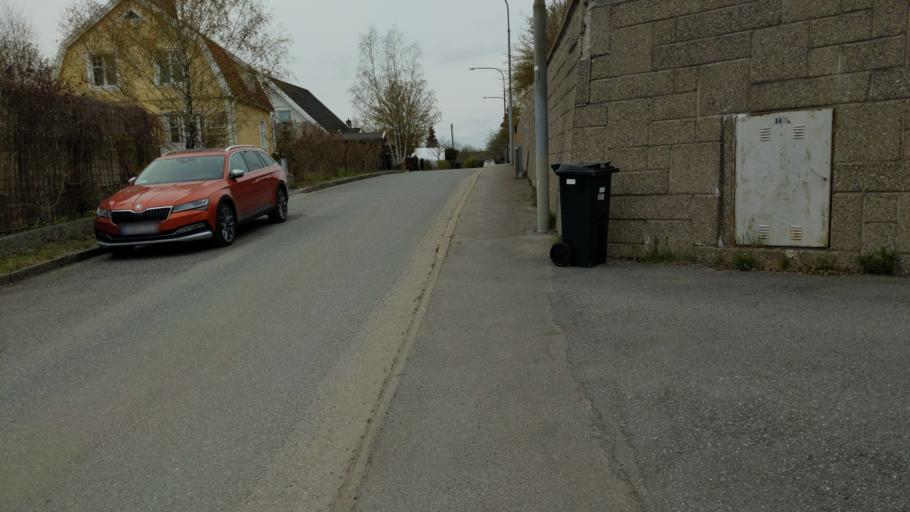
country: SE
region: Stockholm
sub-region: Stockholms Kommun
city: Kista
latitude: 59.3891
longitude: 17.8910
